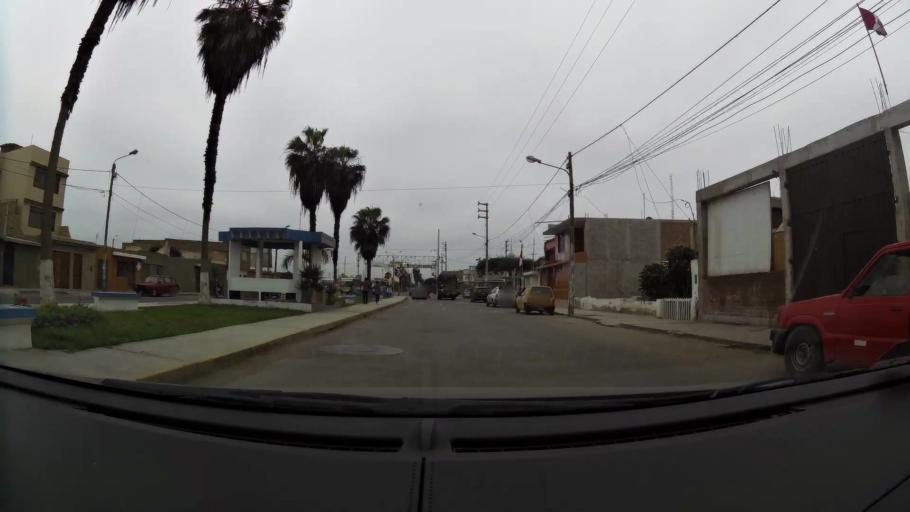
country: PE
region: La Libertad
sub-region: Provincia de Trujillo
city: Buenos Aires
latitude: -8.1412
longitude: -79.0530
